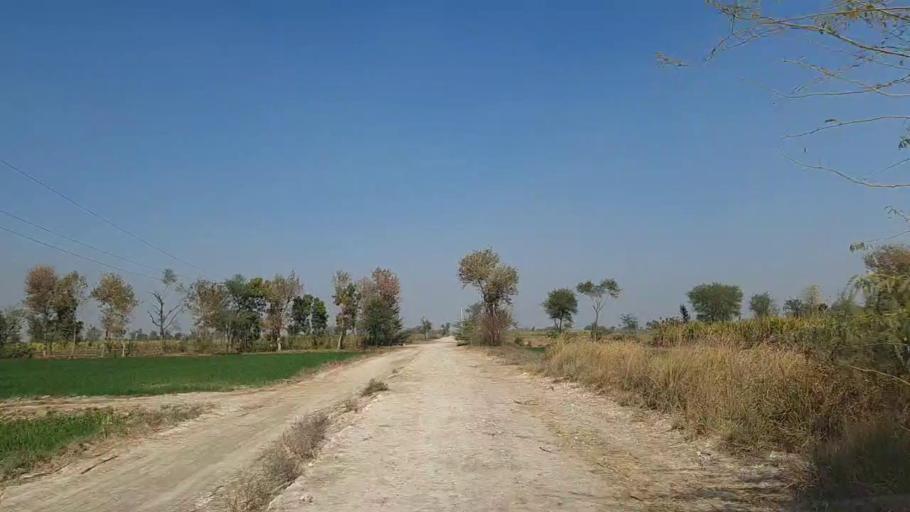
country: PK
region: Sindh
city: Daur
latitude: 26.4881
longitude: 68.3384
